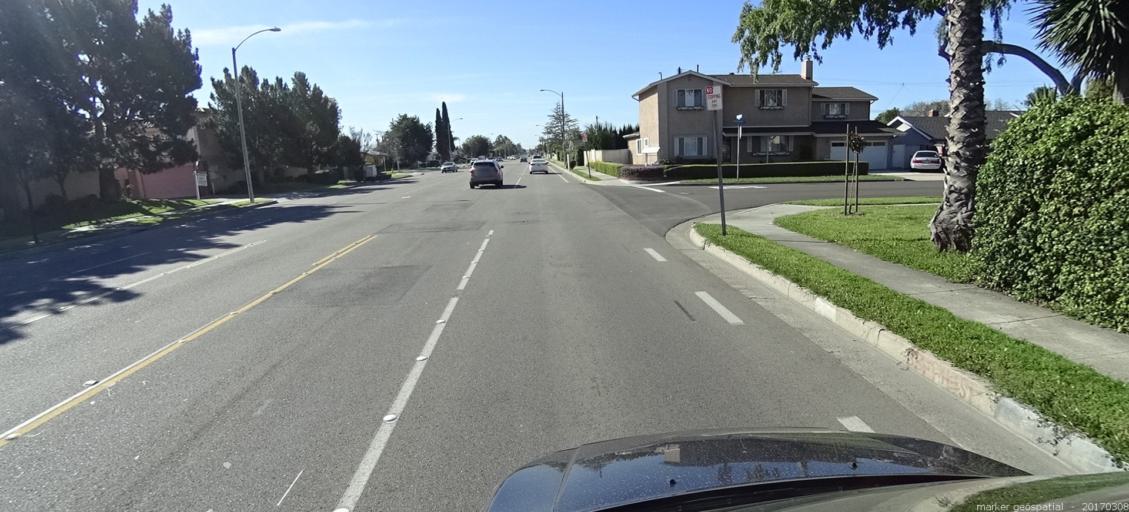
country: US
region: California
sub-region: Orange County
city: Stanton
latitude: 33.8164
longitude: -118.0021
